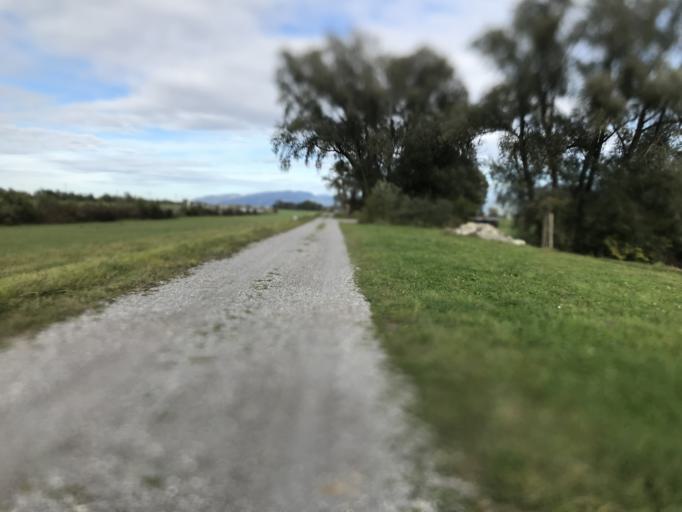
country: AT
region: Vorarlberg
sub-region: Politischer Bezirk Feldkirch
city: Mader
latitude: 47.3667
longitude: 9.6273
